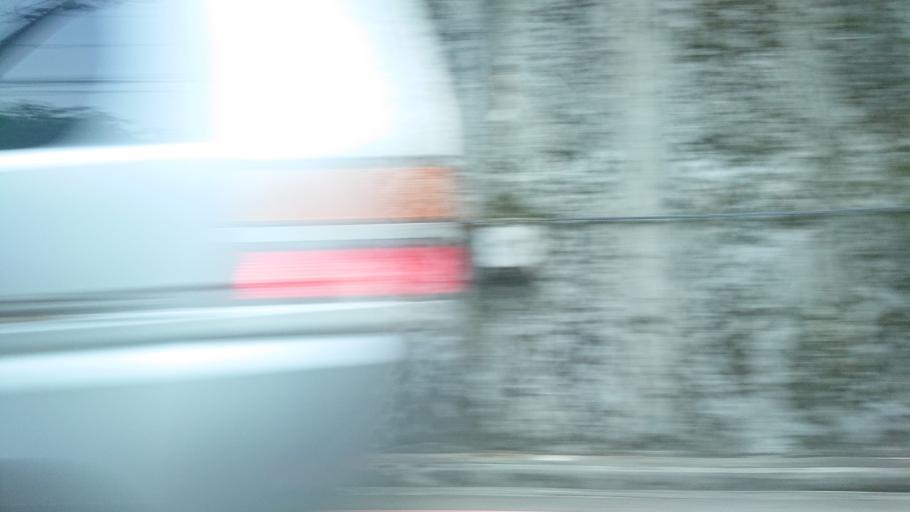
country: TW
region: Taiwan
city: Daxi
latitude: 24.8749
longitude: 121.3860
